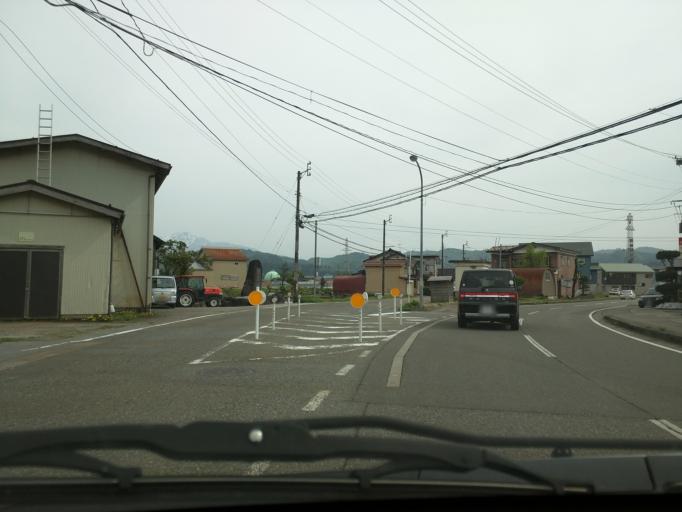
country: JP
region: Niigata
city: Ojiya
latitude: 37.2491
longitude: 138.9304
